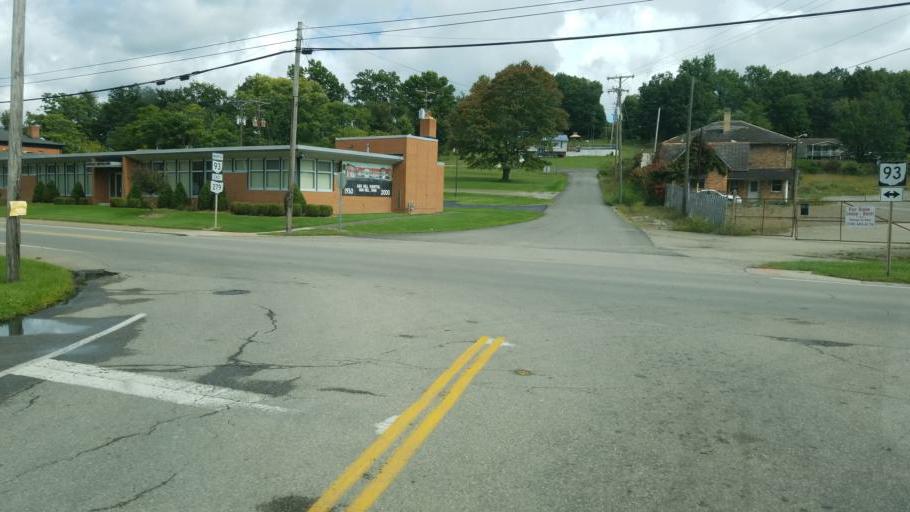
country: US
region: Ohio
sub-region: Jackson County
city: Oak Hill
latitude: 38.8939
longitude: -82.5735
